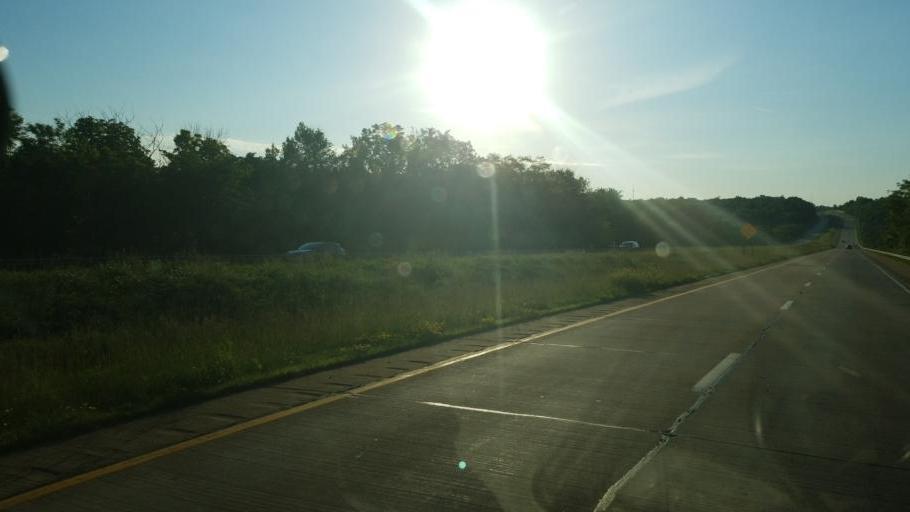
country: US
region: Ohio
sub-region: Ashland County
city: Ashland
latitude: 40.7859
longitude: -82.3303
